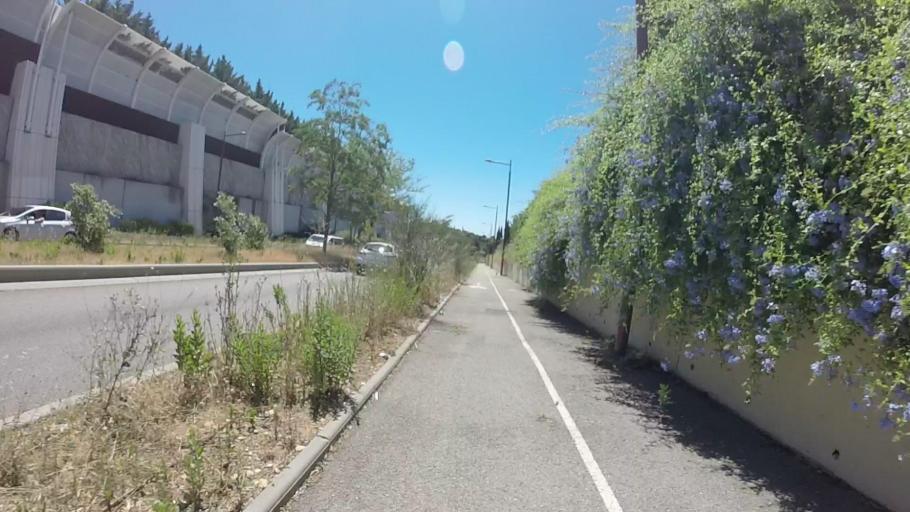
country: FR
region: Provence-Alpes-Cote d'Azur
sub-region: Departement des Alpes-Maritimes
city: Biot
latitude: 43.5934
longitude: 7.0914
